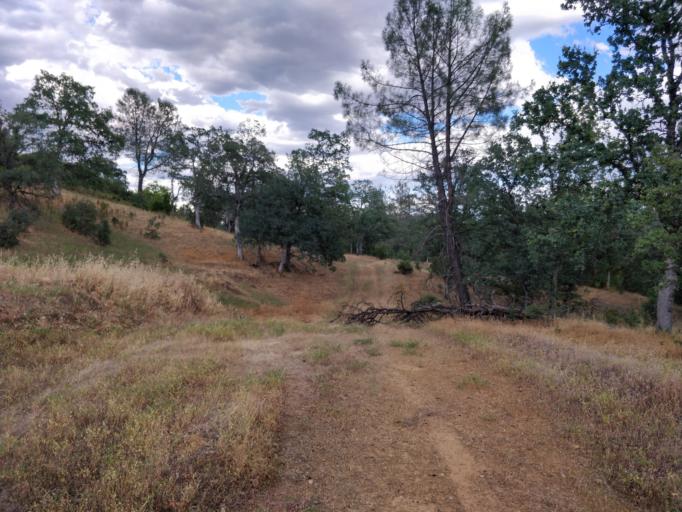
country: US
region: California
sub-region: Shasta County
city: Redding
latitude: 40.6099
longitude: -122.3857
